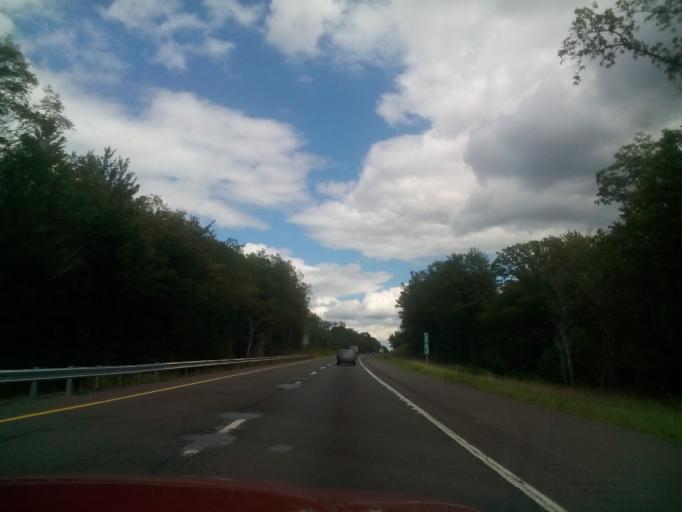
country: US
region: Pennsylvania
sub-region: Luzerne County
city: White Haven
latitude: 41.0743
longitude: -75.6772
